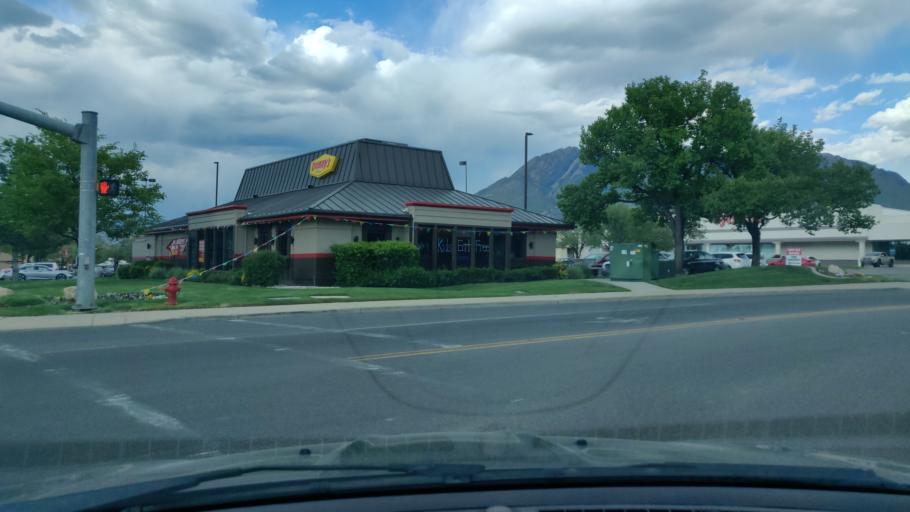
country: US
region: Utah
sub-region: Salt Lake County
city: Little Cottonwood Creek Valley
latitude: 40.6234
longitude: -111.8555
